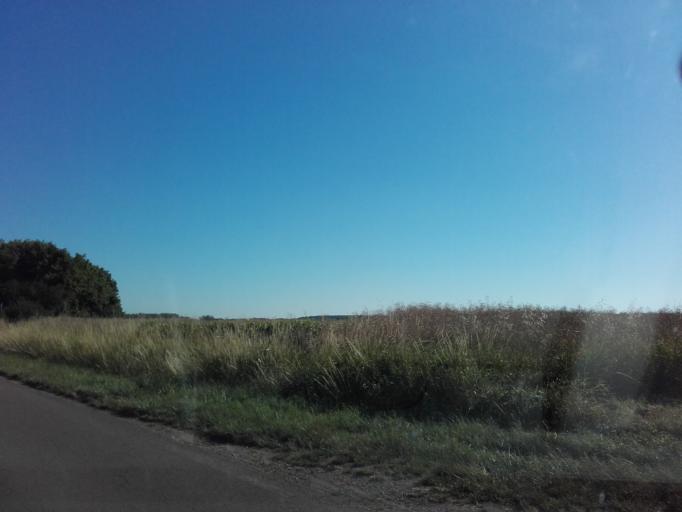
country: FR
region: Bourgogne
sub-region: Departement de Saone-et-Loire
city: Rully
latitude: 46.8689
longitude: 4.7545
